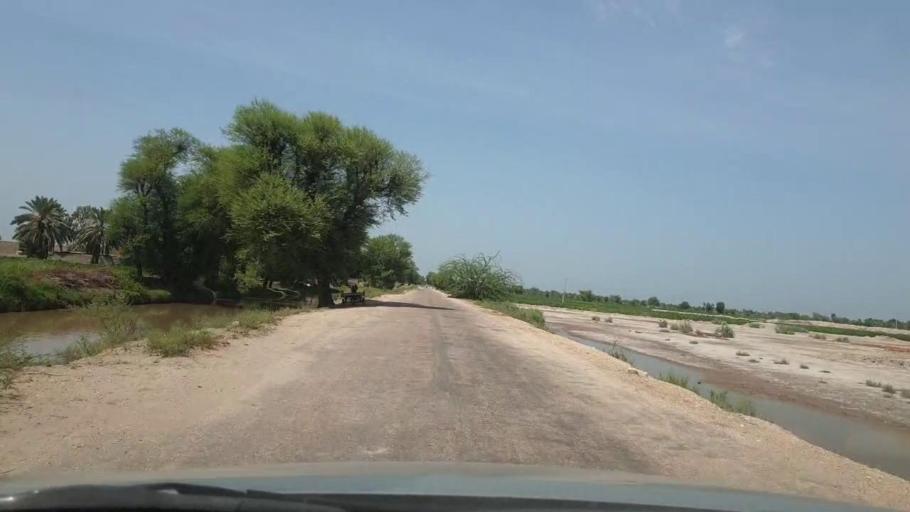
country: PK
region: Sindh
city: Pano Aqil
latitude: 27.6734
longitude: 69.1089
